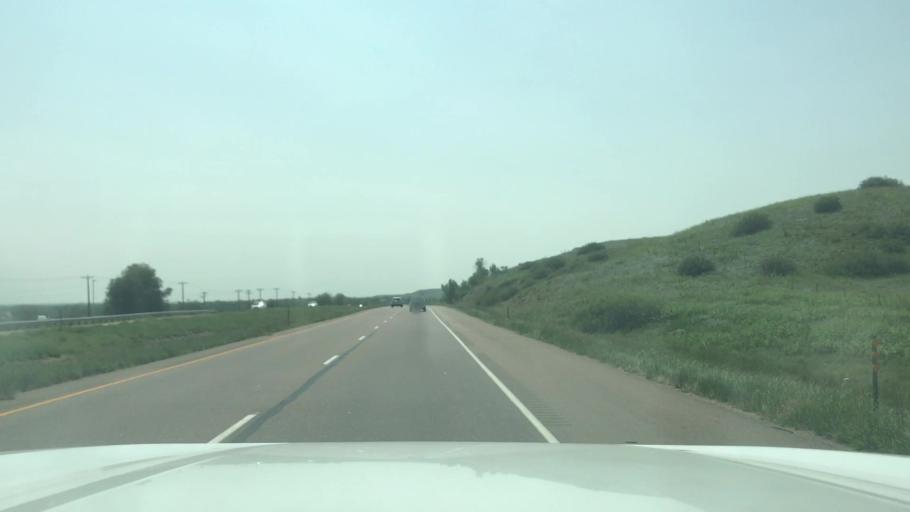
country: US
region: Colorado
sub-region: El Paso County
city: Fountain
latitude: 38.6920
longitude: -104.7197
